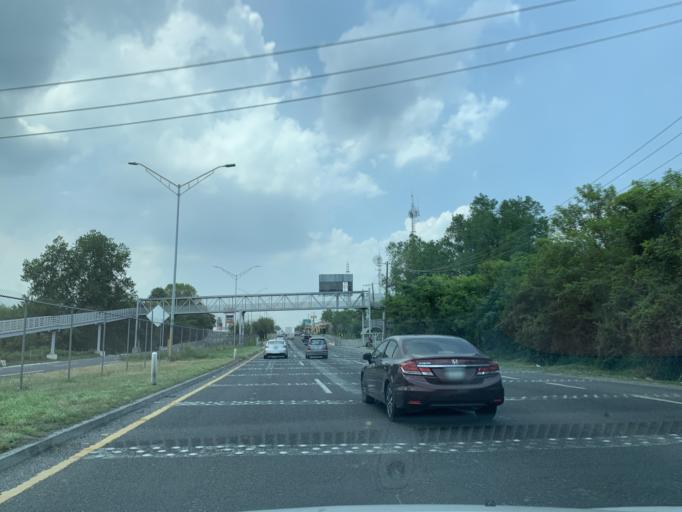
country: MX
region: Nuevo Leon
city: Santiago
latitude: 25.4929
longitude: -100.1866
